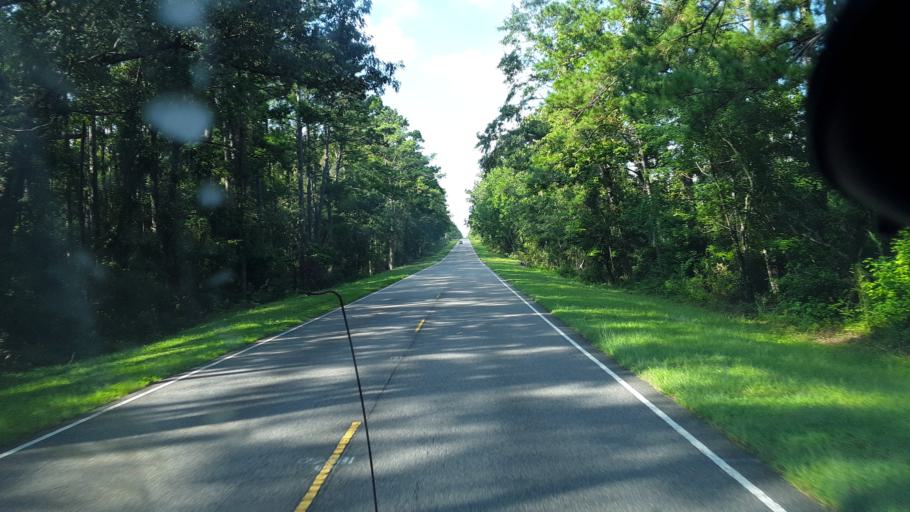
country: US
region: North Carolina
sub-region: Brunswick County
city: Boiling Spring Lakes
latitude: 34.0403
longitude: -78.0071
